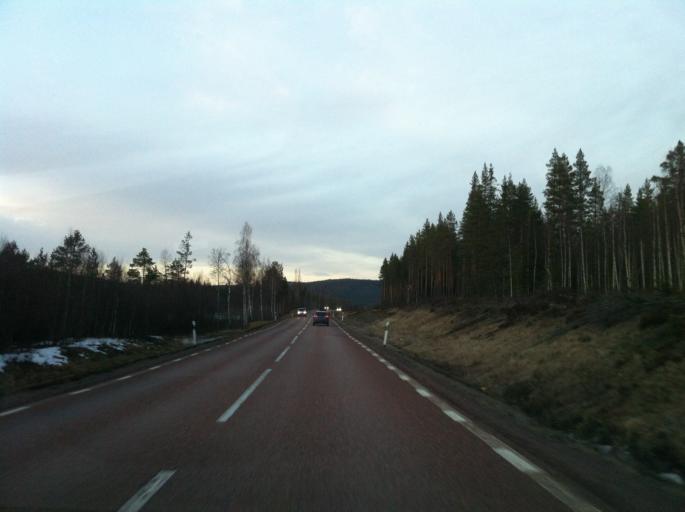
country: SE
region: Dalarna
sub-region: Mora Kommun
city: Mora
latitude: 60.8729
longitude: 14.3688
